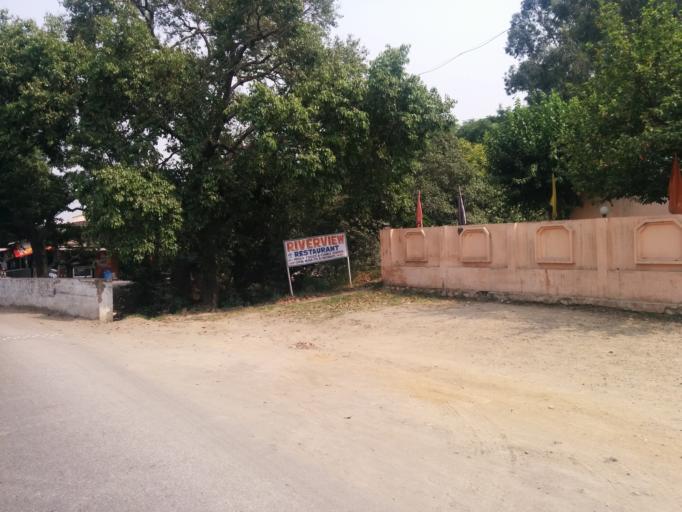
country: IN
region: Punjab
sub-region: Pathankot
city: Pathankot
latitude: 32.2625
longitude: 75.5893
